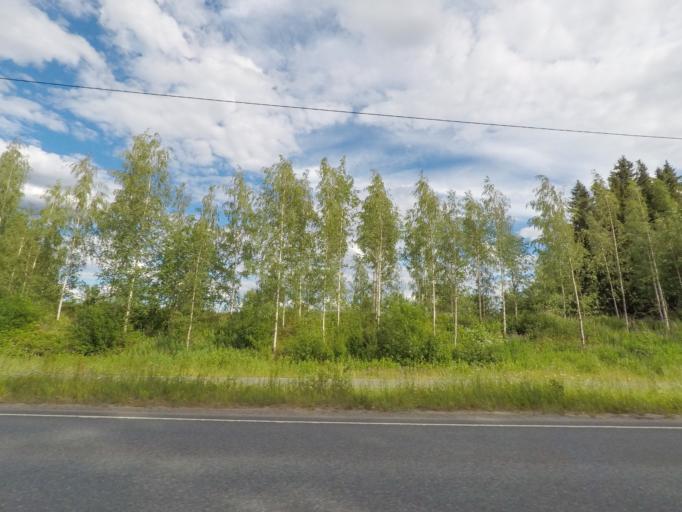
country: FI
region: Paijanne Tavastia
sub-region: Lahti
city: Lahti
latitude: 60.9495
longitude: 25.6099
